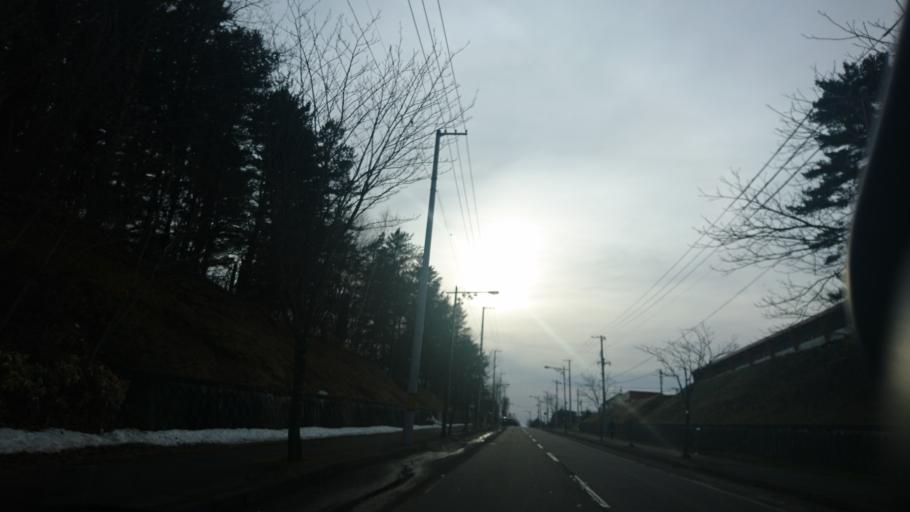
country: JP
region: Hokkaido
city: Otofuke
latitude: 42.9967
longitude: 143.1952
